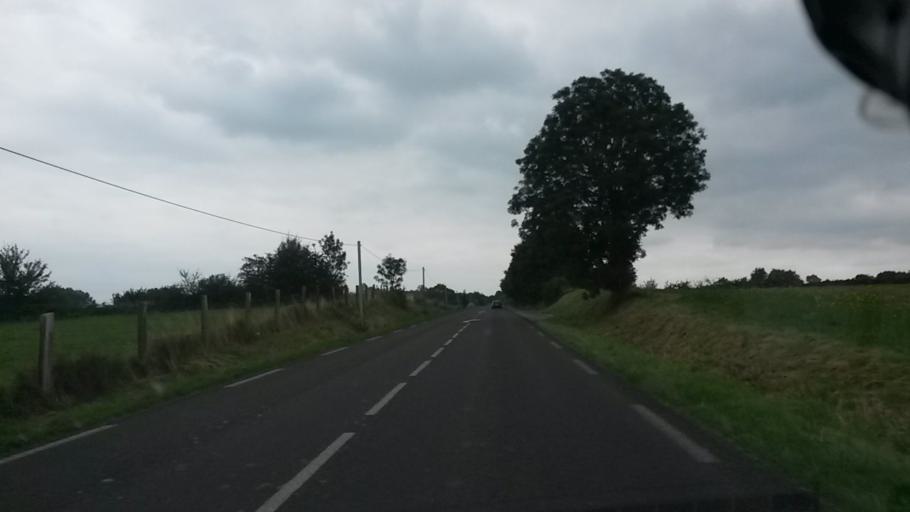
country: FR
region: Haute-Normandie
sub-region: Departement de la Seine-Maritime
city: Gaillefontaine
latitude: 49.6465
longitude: 1.6167
